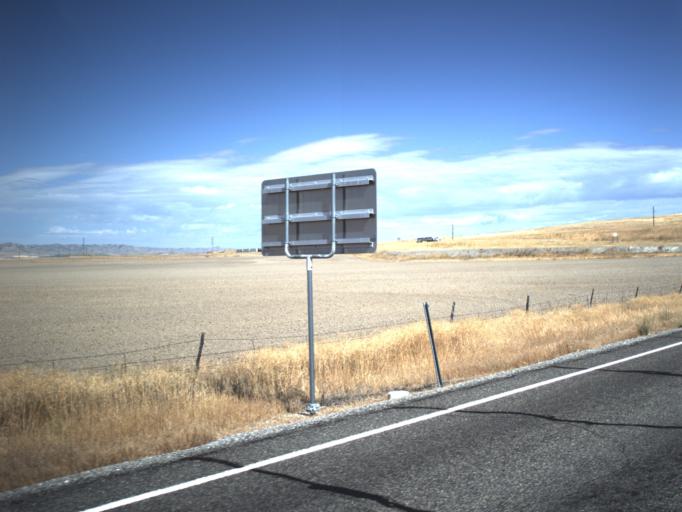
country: US
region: Utah
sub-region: Box Elder County
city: Garland
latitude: 41.8140
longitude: -112.4143
